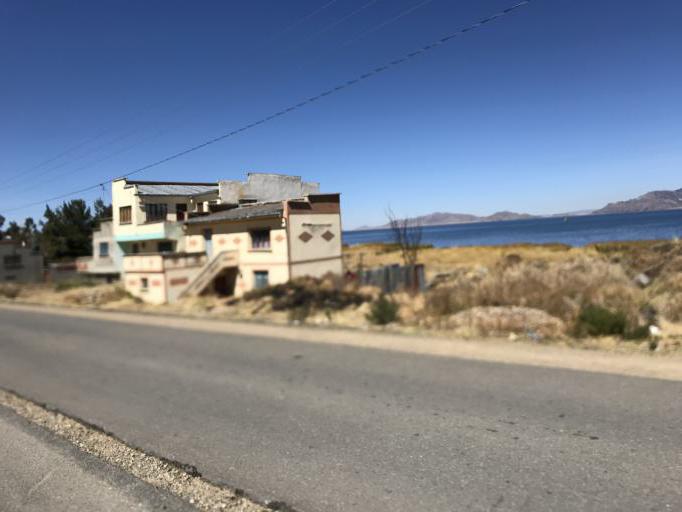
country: BO
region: La Paz
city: Huatajata
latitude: -16.2148
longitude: -68.6776
